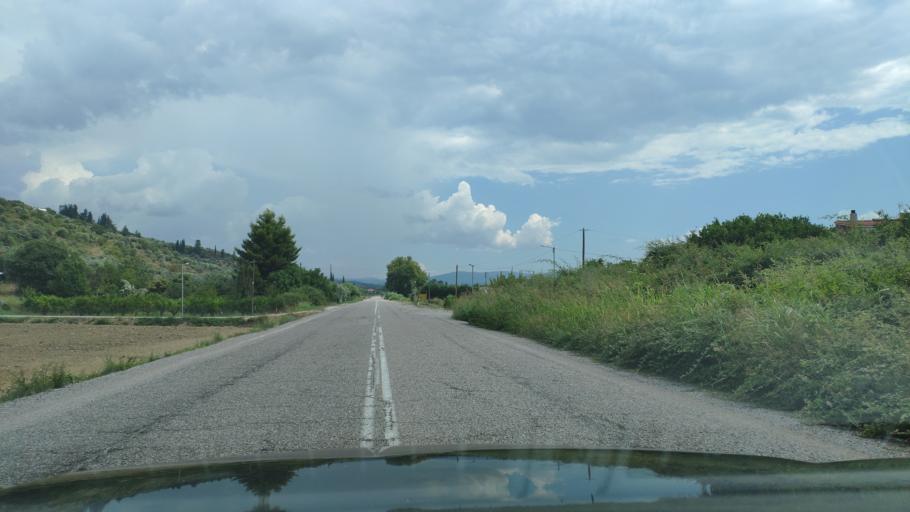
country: GR
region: West Greece
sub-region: Nomos Aitolias kai Akarnanias
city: Krikellos
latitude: 38.9616
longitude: 21.1715
